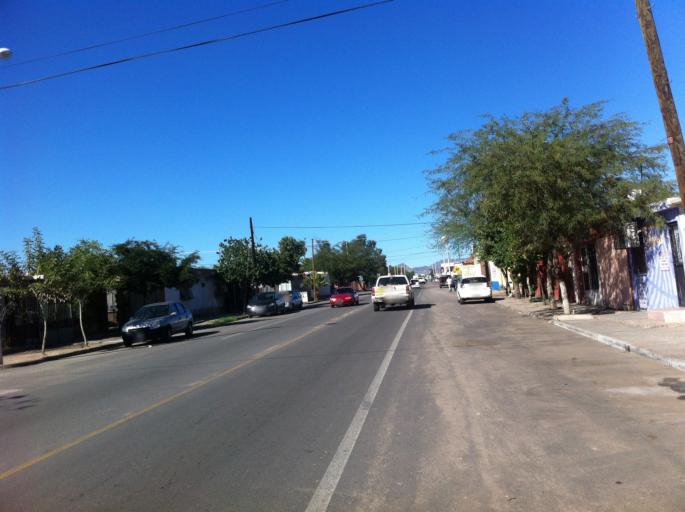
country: MX
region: Sonora
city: Hermosillo
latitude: 29.1068
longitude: -111.0055
